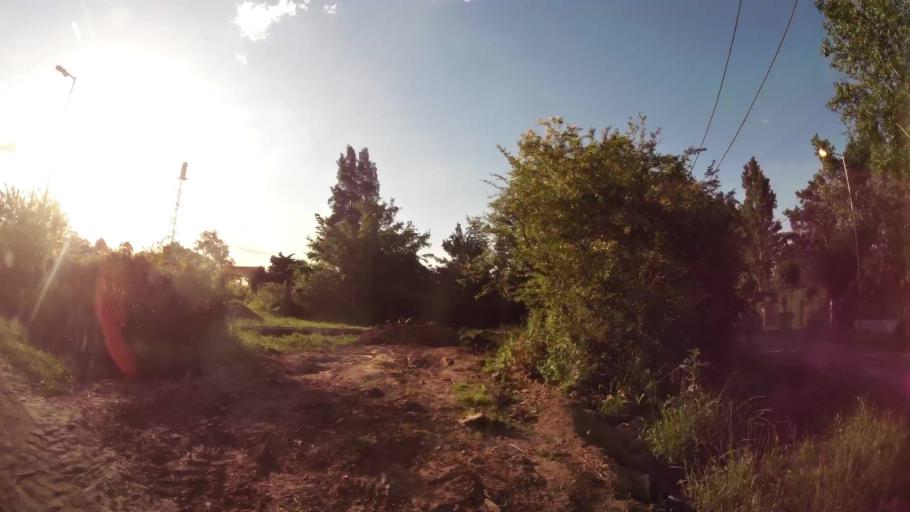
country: AR
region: Buenos Aires
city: Santa Catalina - Dique Lujan
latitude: -34.4727
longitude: -58.7484
